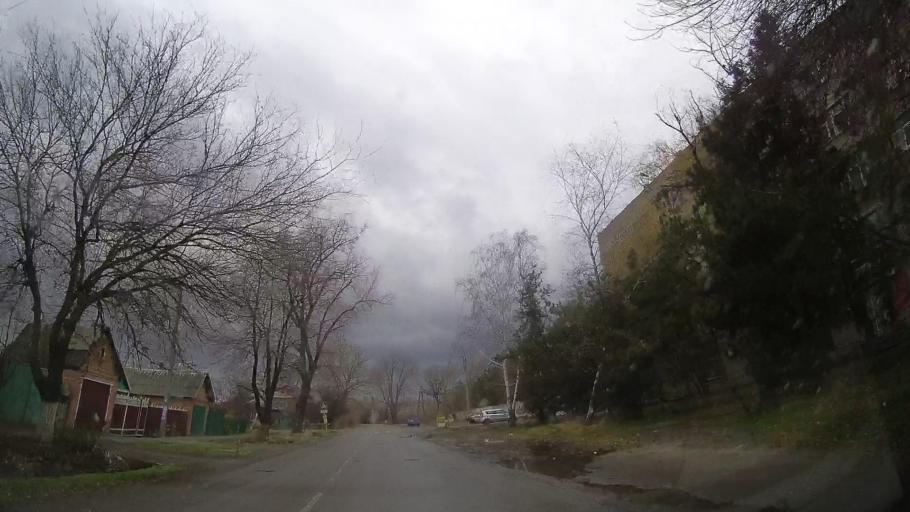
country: RU
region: Rostov
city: Bataysk
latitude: 47.1130
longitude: 39.7394
